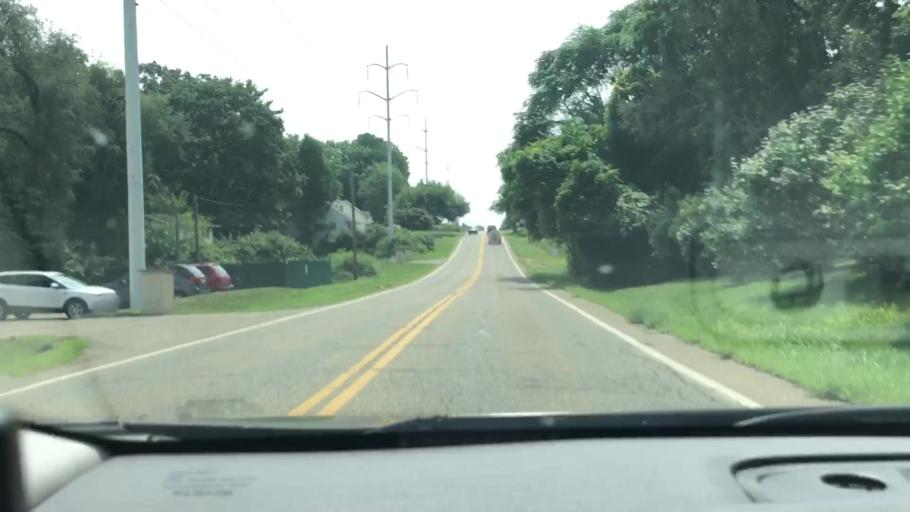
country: US
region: Ohio
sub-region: Stark County
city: Perry Heights
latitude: 40.8191
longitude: -81.4347
